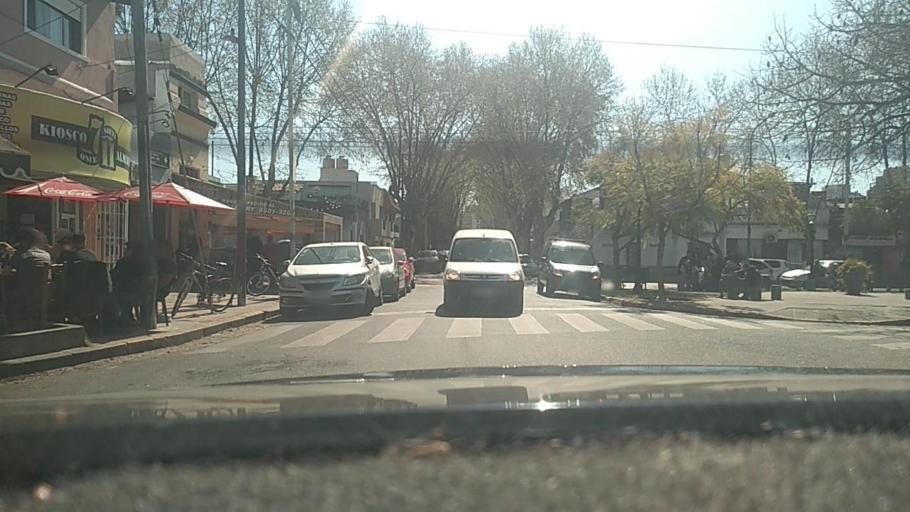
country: AR
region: Buenos Aires F.D.
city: Villa Santa Rita
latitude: -34.6028
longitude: -58.4830
